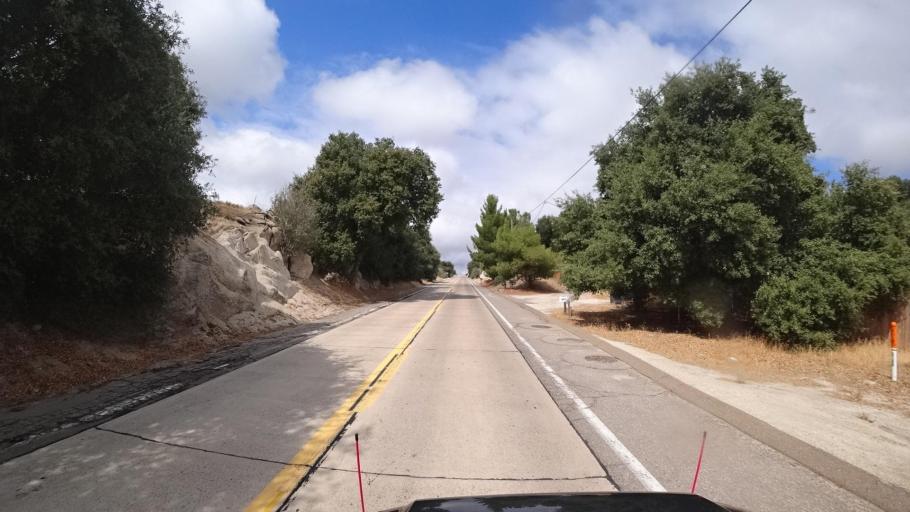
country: US
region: California
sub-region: San Diego County
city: Campo
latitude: 32.6882
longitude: -116.3375
